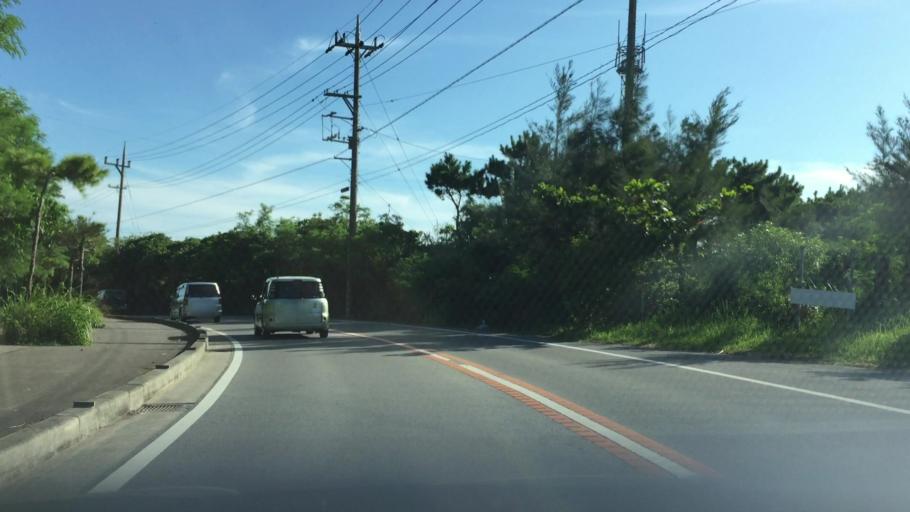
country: JP
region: Okinawa
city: Ishigaki
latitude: 24.4412
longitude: 124.1181
